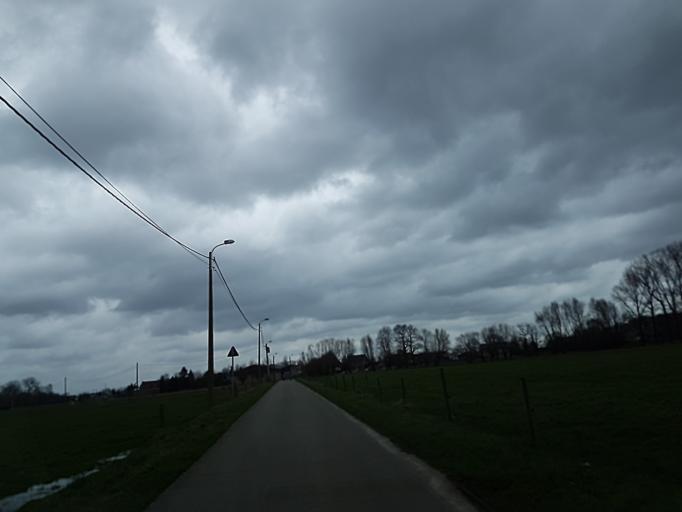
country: BE
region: Flanders
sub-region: Provincie Vlaams-Brabant
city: Kapelle-op-den-Bos
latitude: 51.0058
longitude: 4.3965
